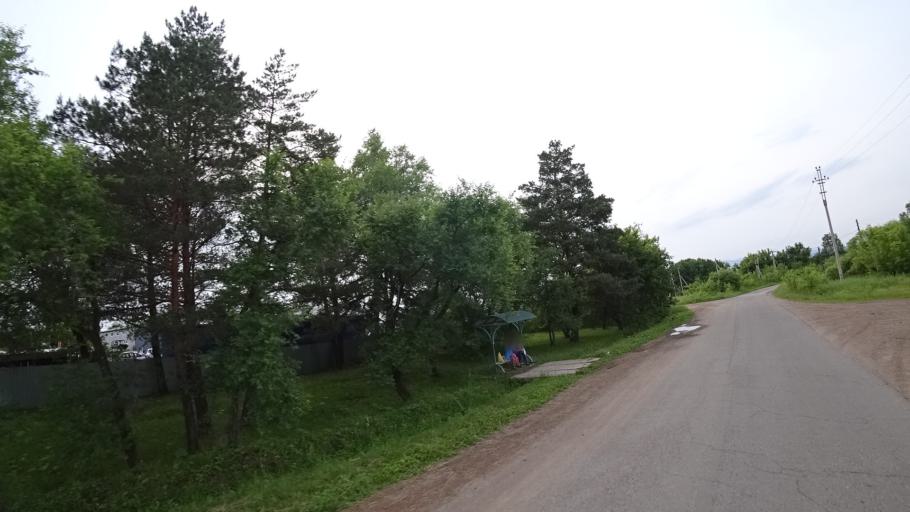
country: RU
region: Primorskiy
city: Novosysoyevka
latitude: 44.2433
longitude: 133.3674
